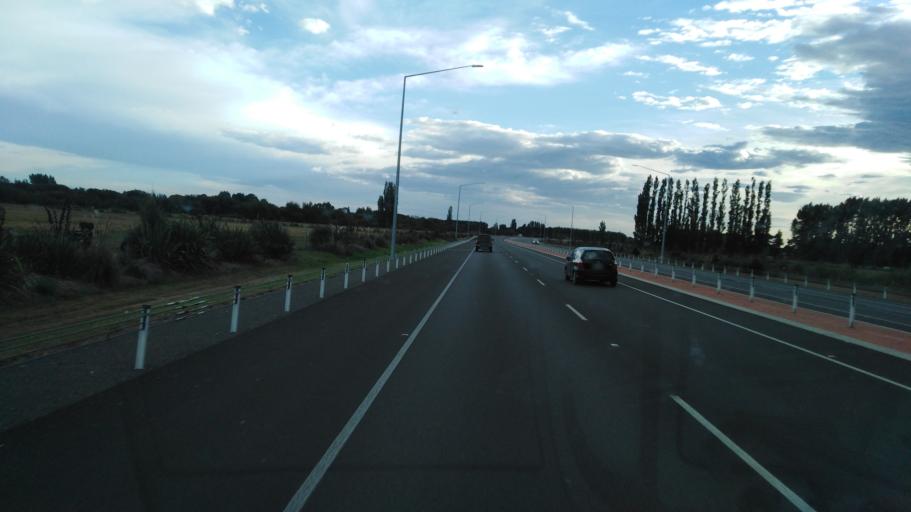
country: NZ
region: Canterbury
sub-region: Waimakariri District
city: Kaiapoi
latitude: -43.4446
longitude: 172.6160
